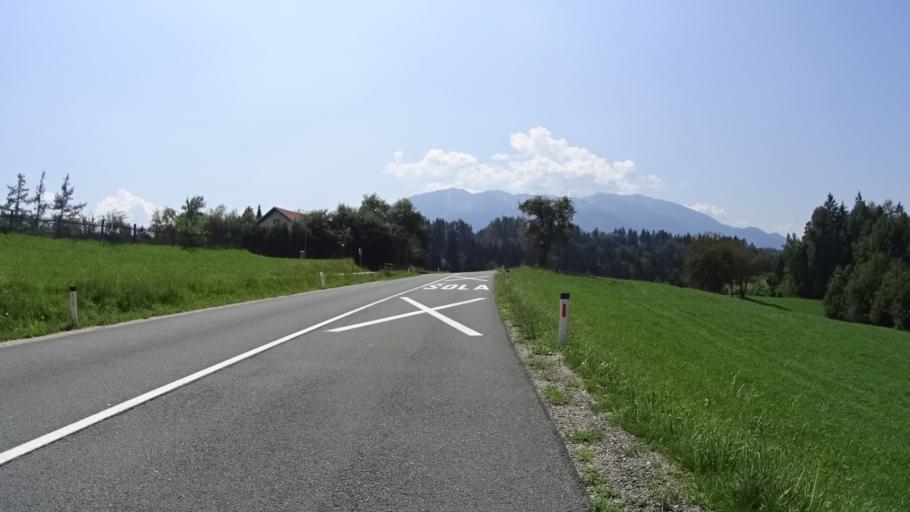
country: SI
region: Mezica
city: Mezica
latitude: 46.5621
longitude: 14.8498
